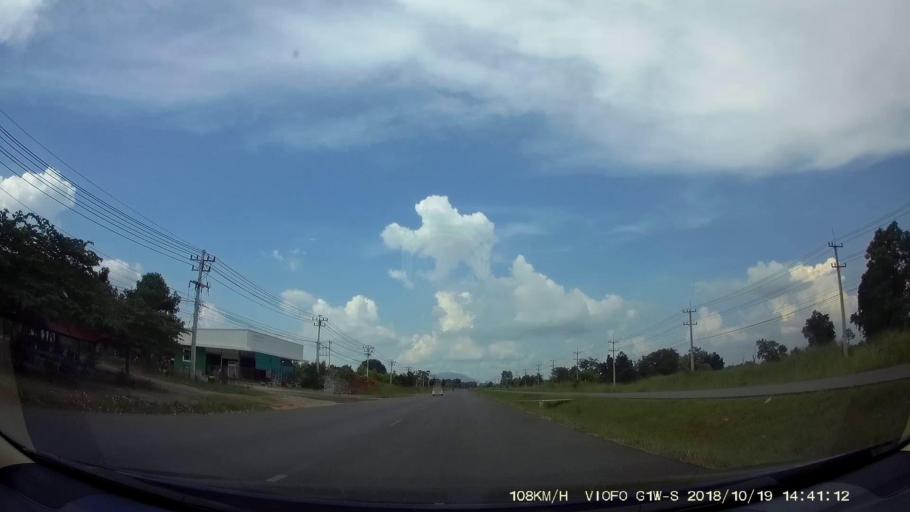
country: TH
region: Chaiyaphum
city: Phu Khiao
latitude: 16.2530
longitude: 102.1983
